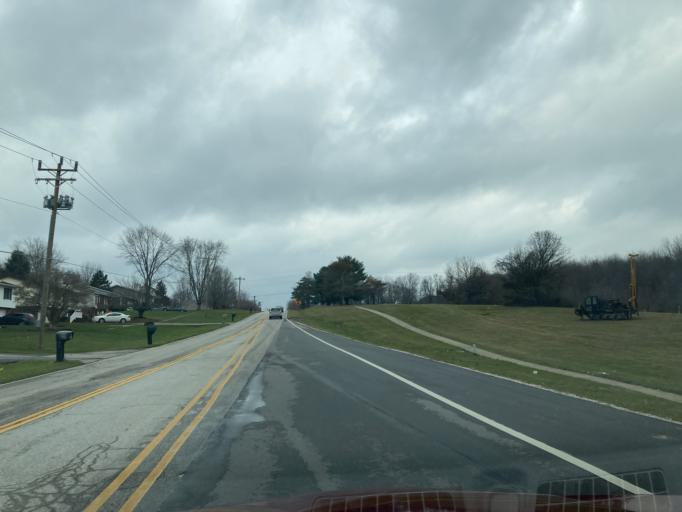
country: US
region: Indiana
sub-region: Monroe County
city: Bloomington
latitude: 39.1217
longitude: -86.5418
